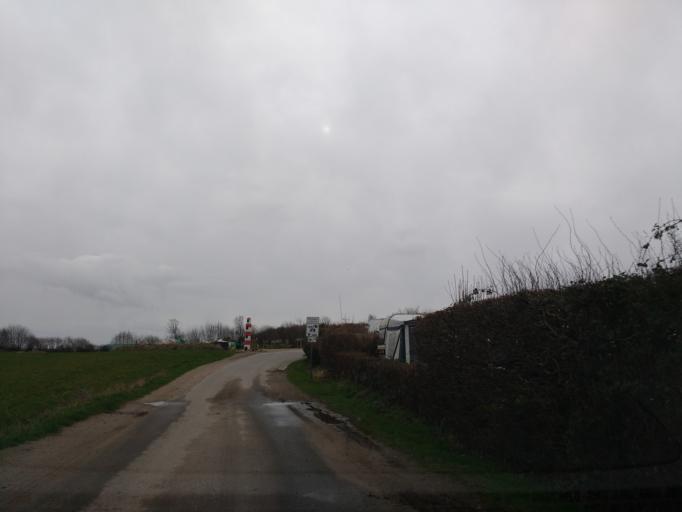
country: DE
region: Schleswig-Holstein
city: Schashagen
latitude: 54.1204
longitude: 10.9227
